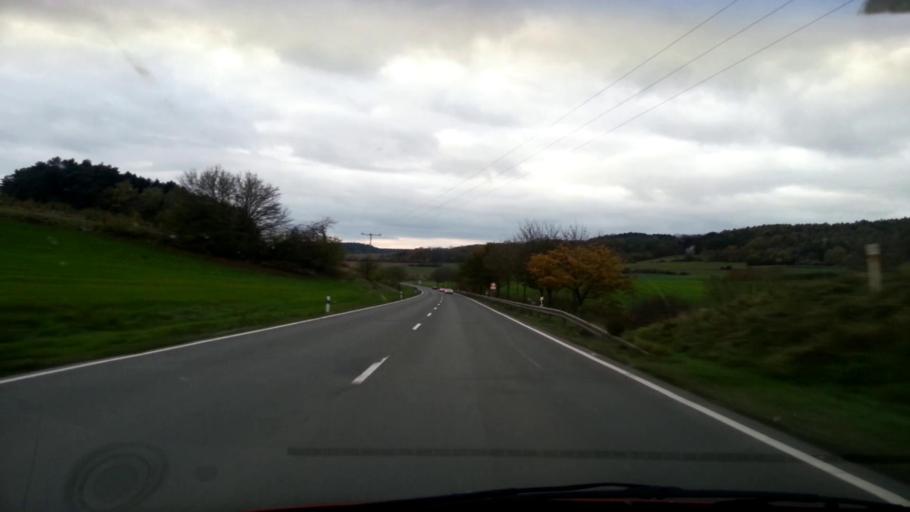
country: DE
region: Bavaria
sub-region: Upper Franconia
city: Kueps Oberfranken
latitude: 50.2117
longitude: 11.2469
